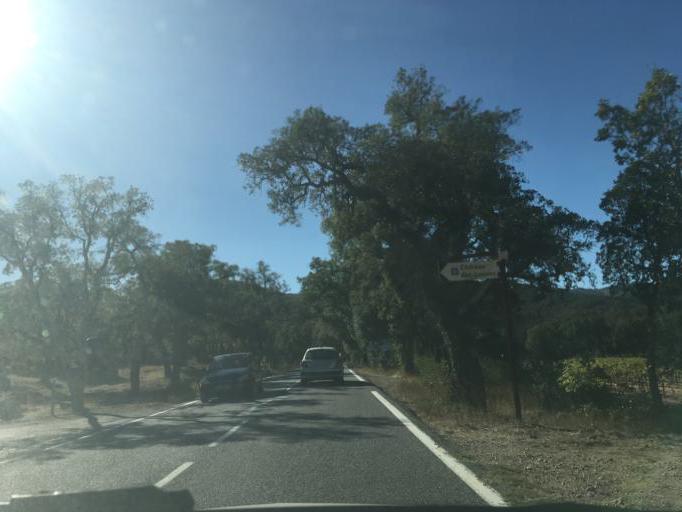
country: FR
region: Provence-Alpes-Cote d'Azur
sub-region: Departement du Var
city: La Garde-Freinet
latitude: 43.3365
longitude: 6.4270
